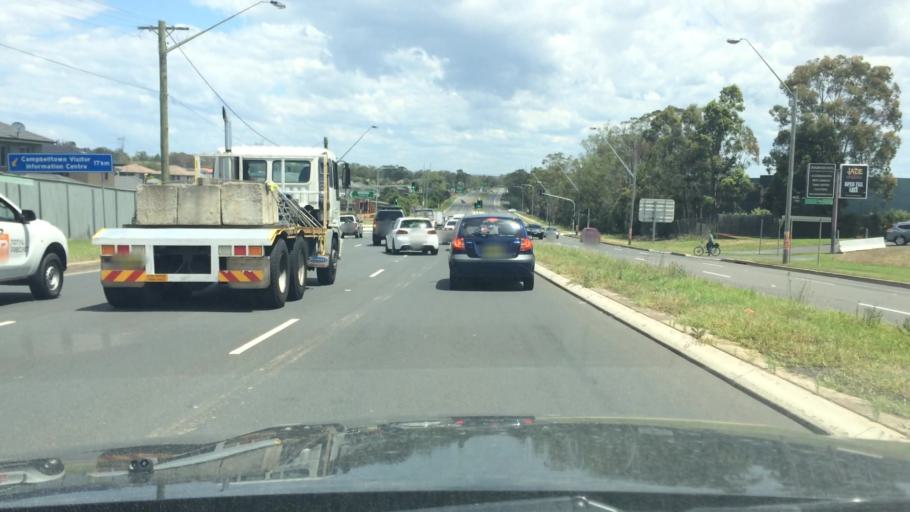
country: AU
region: New South Wales
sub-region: Campbelltown Municipality
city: Glenfield
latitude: -33.9587
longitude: 150.8864
